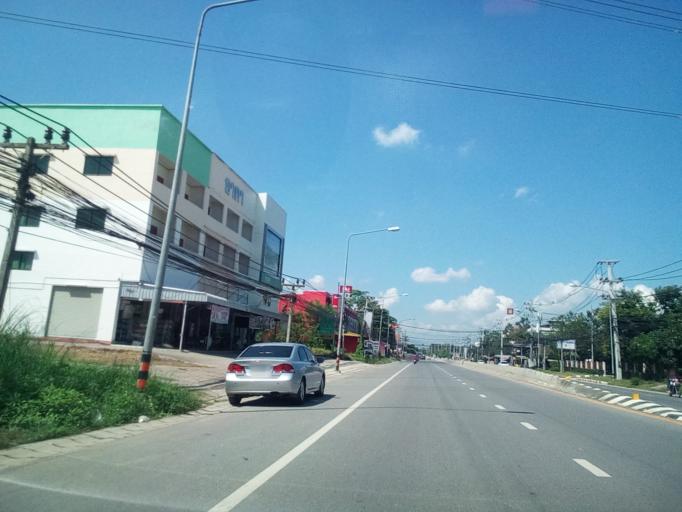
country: TH
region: Lamphun
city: Lamphun
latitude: 18.5856
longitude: 99.0530
